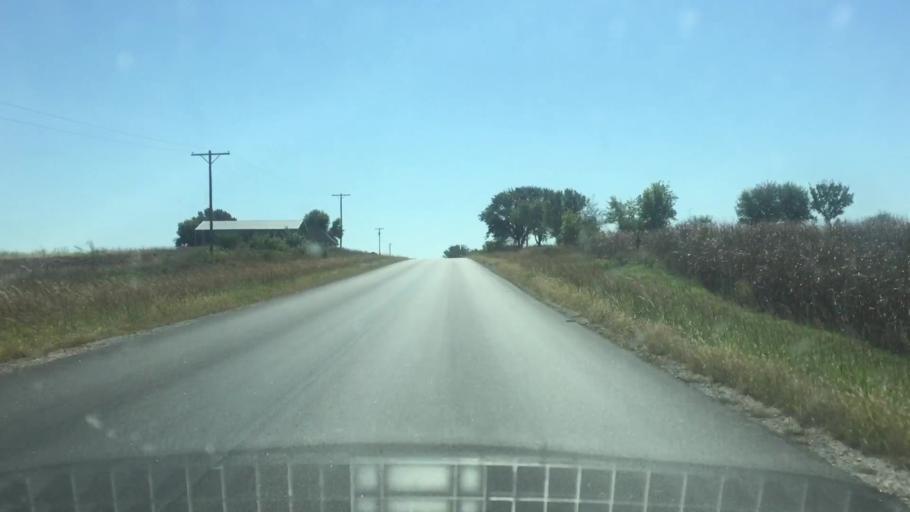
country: US
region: Kansas
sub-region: Marshall County
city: Marysville
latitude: 39.9550
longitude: -96.6009
